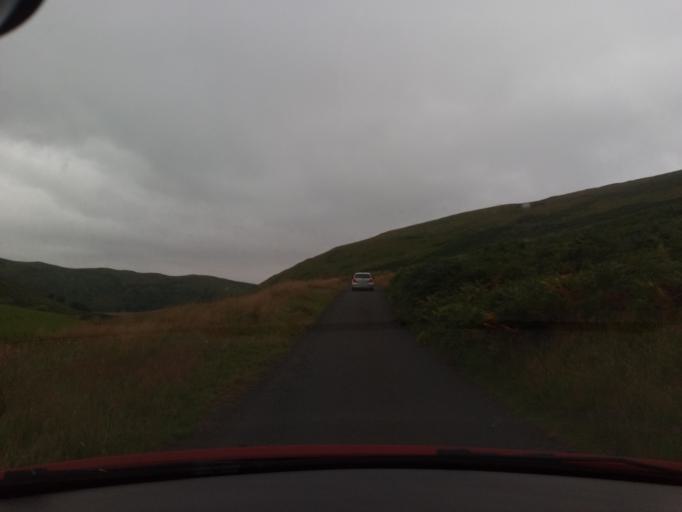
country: GB
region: England
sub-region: Northumberland
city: Rochester
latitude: 55.3624
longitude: -2.1814
